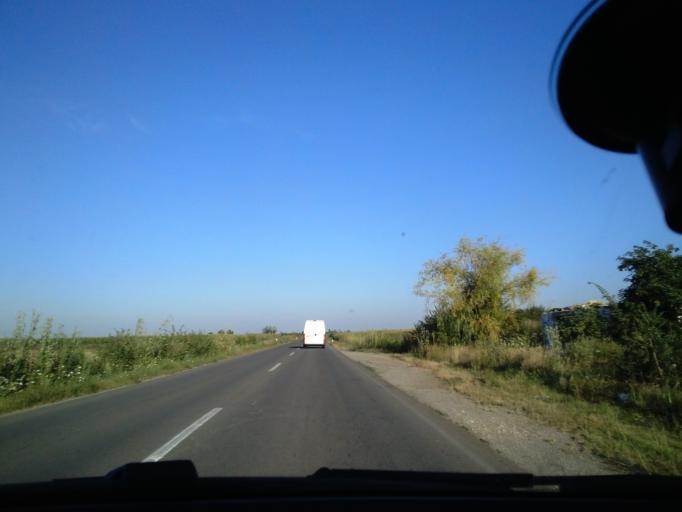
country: RS
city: Obrovac
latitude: 45.4060
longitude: 19.4256
